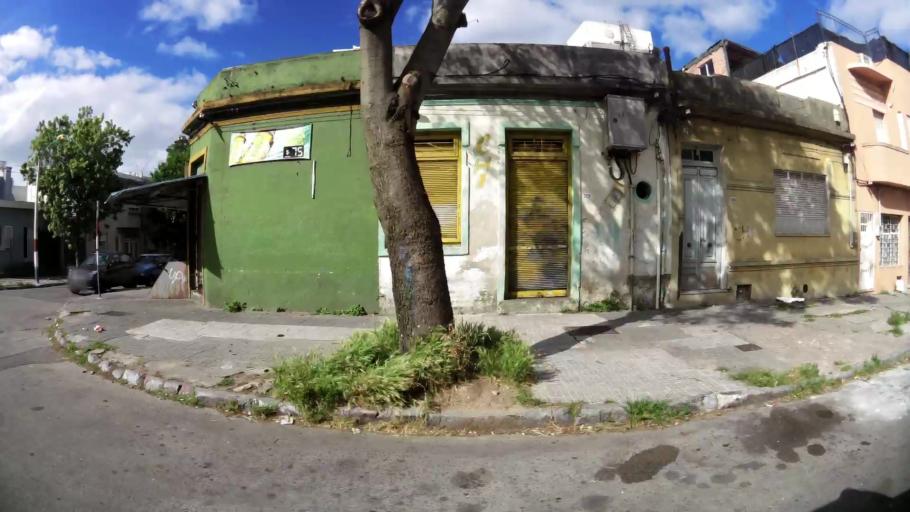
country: UY
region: Montevideo
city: Montevideo
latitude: -34.8852
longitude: -56.1611
